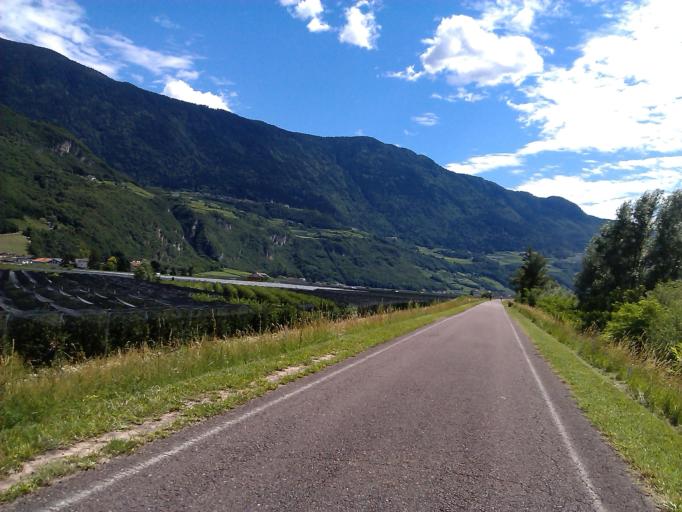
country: IT
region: Trentino-Alto Adige
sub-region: Bolzano
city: Laghetti
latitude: 46.2743
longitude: 11.2354
